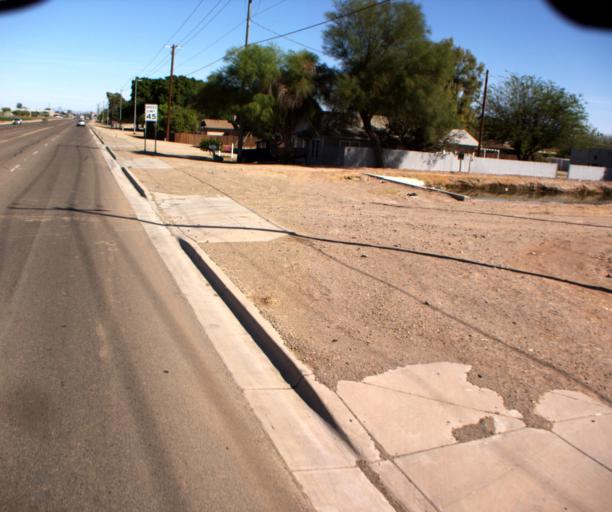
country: US
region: Arizona
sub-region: Yuma County
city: Yuma
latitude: 32.6619
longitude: -114.6501
